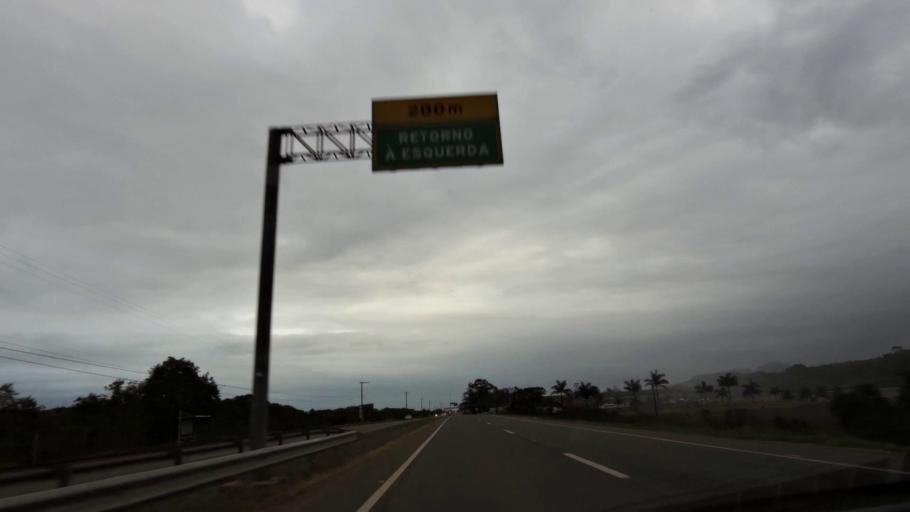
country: BR
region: Espirito Santo
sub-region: Guarapari
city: Guarapari
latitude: -20.5353
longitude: -40.3874
